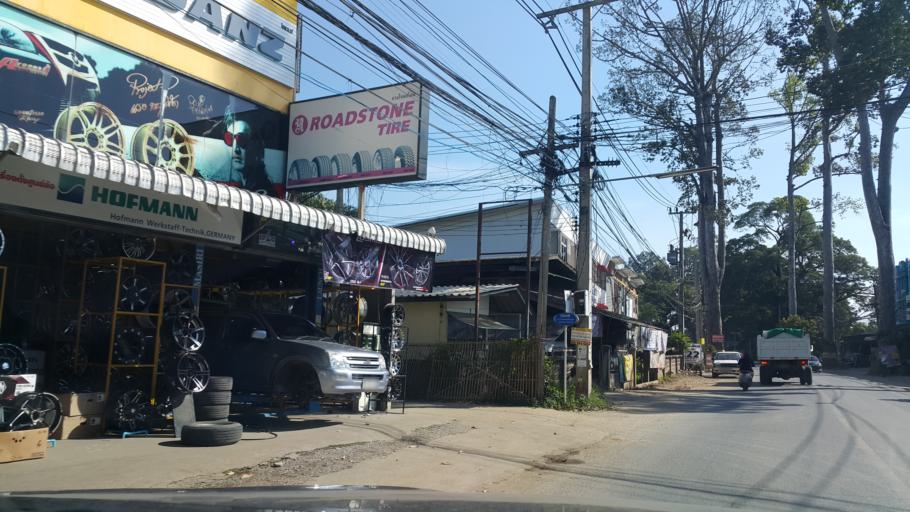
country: TH
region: Chiang Mai
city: Saraphi
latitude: 18.7422
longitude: 99.0140
